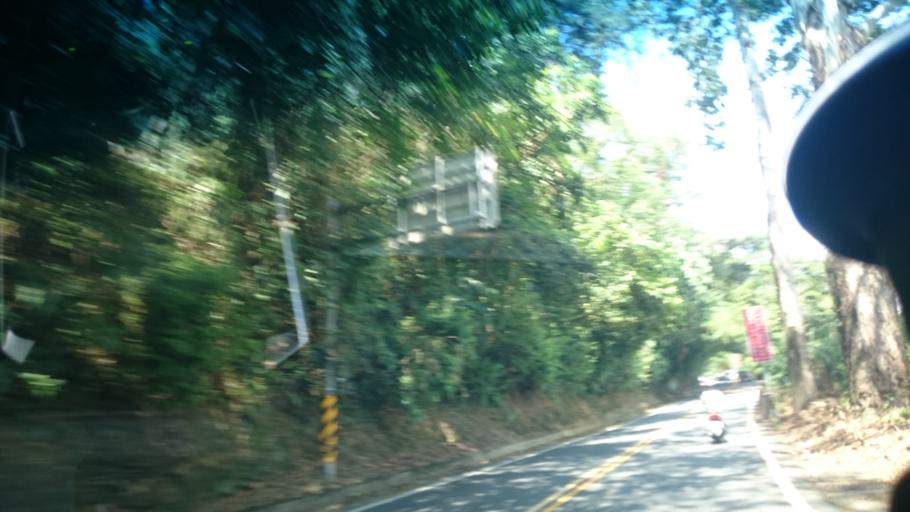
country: TW
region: Taiwan
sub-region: Nantou
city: Puli
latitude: 24.0247
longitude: 121.1347
